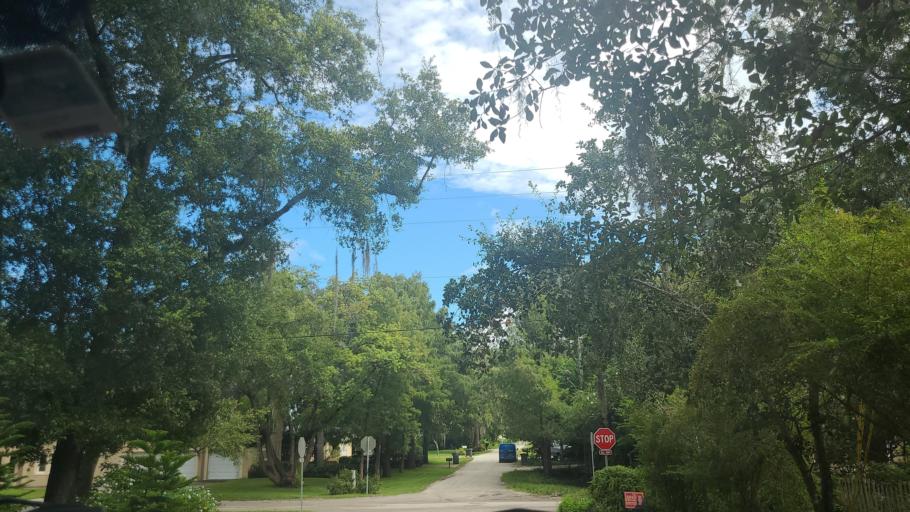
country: US
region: Florida
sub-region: Orange County
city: Windermere
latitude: 28.4986
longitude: -81.5375
